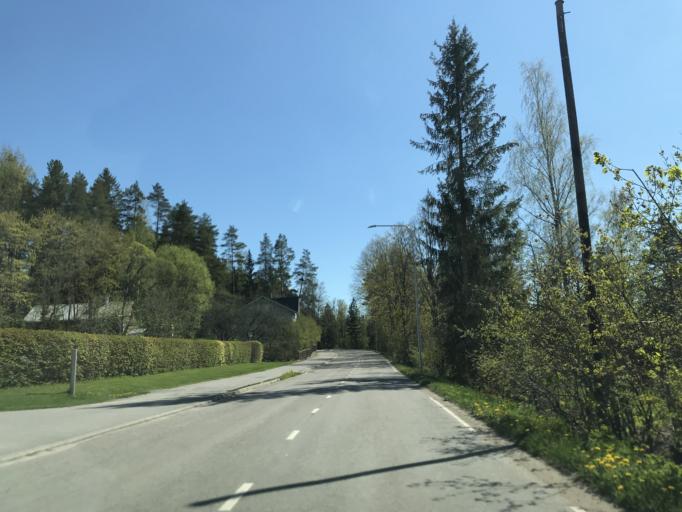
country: FI
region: Paijanne Tavastia
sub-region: Lahti
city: Orimattila
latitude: 60.8135
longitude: 25.7341
